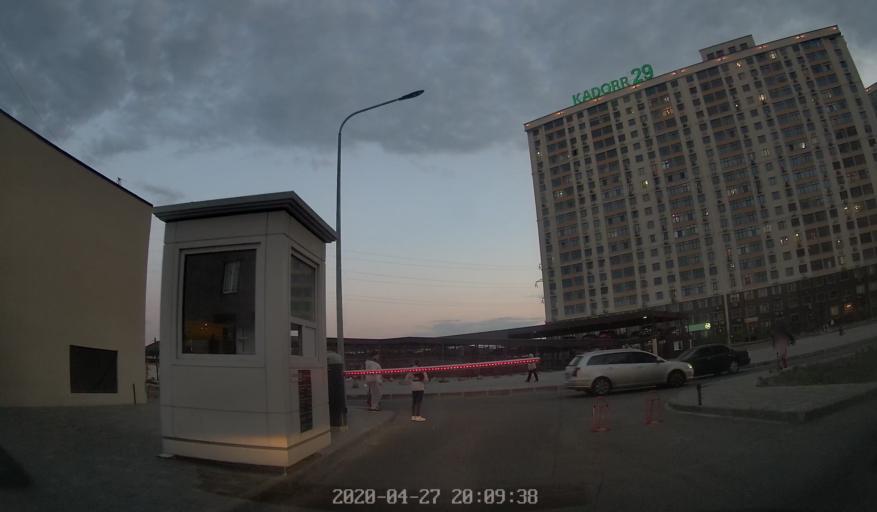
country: NE
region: Zinder
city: Mirriah
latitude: 13.9145
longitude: 9.2133
